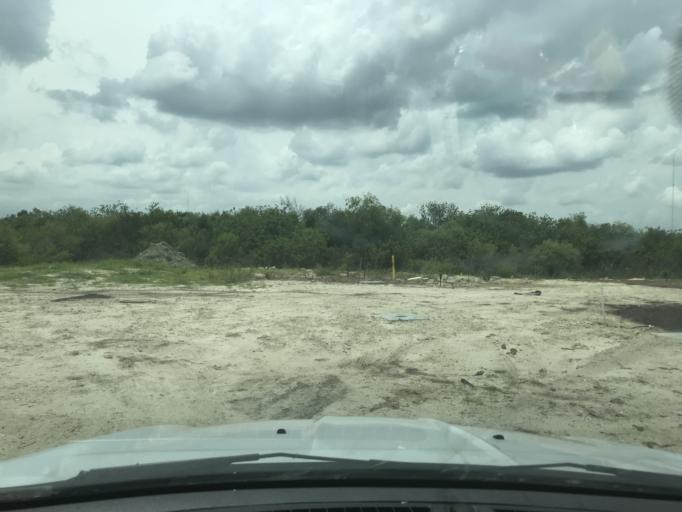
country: US
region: Florida
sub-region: Lee County
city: Olga
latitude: 26.7775
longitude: -81.7450
